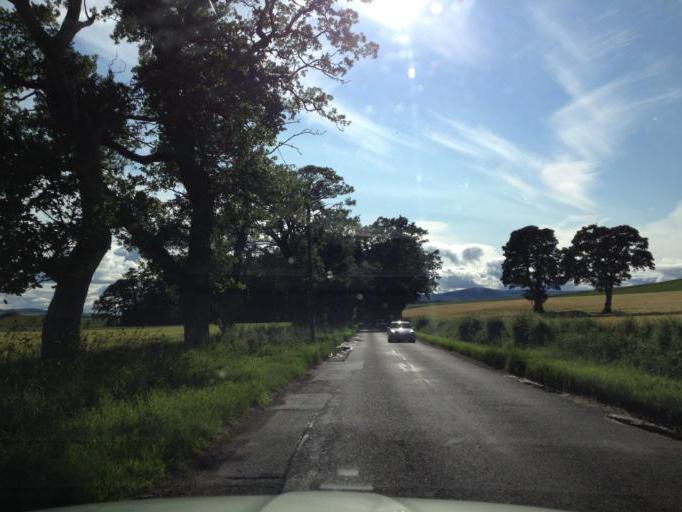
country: GB
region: Scotland
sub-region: Aberdeenshire
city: Laurencekirk
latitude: 56.8441
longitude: -2.5929
